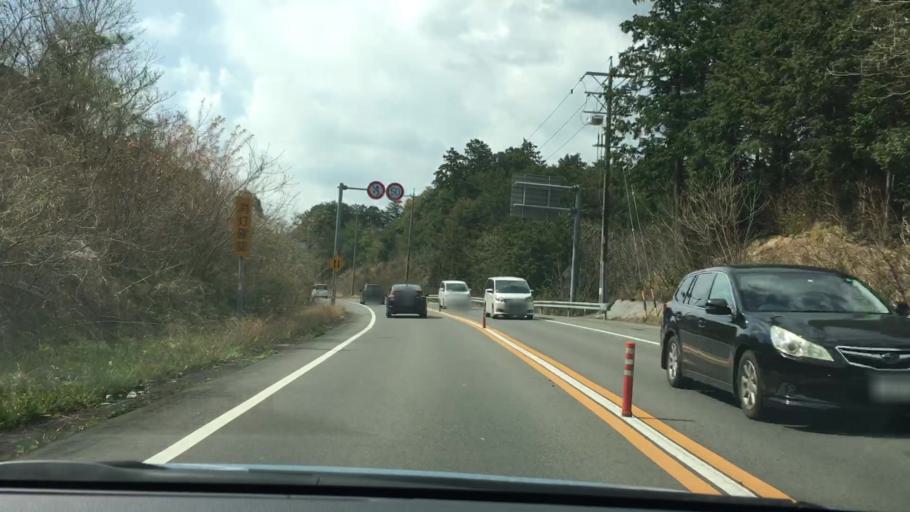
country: JP
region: Mie
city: Toba
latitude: 34.4894
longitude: 136.8122
